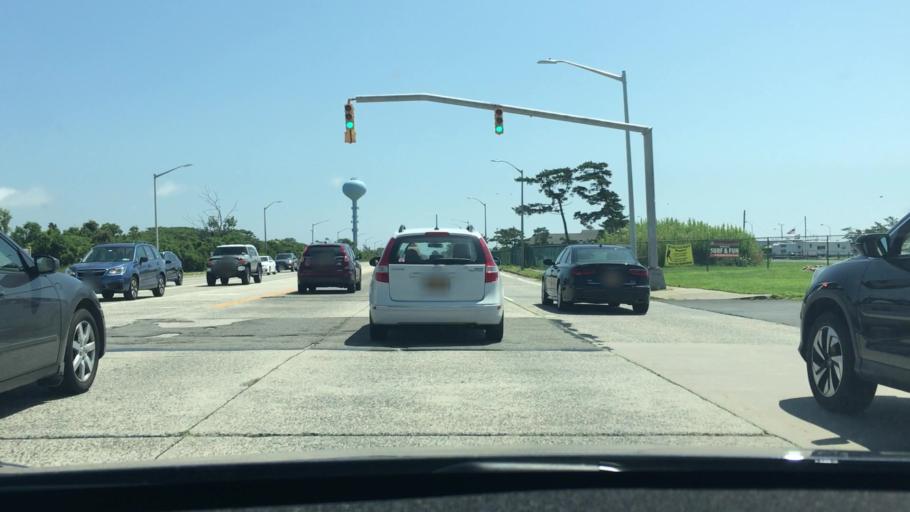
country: US
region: New York
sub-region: Nassau County
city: Point Lookout
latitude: 40.5919
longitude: -73.6014
